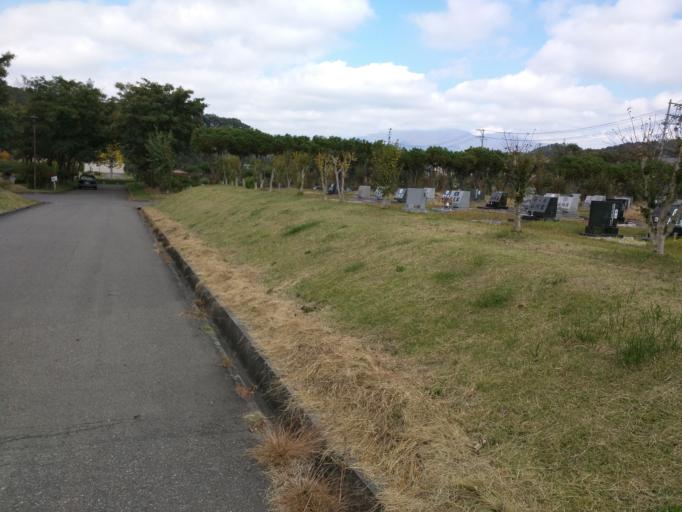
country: JP
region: Fukushima
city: Kitakata
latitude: 37.5139
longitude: 139.9459
